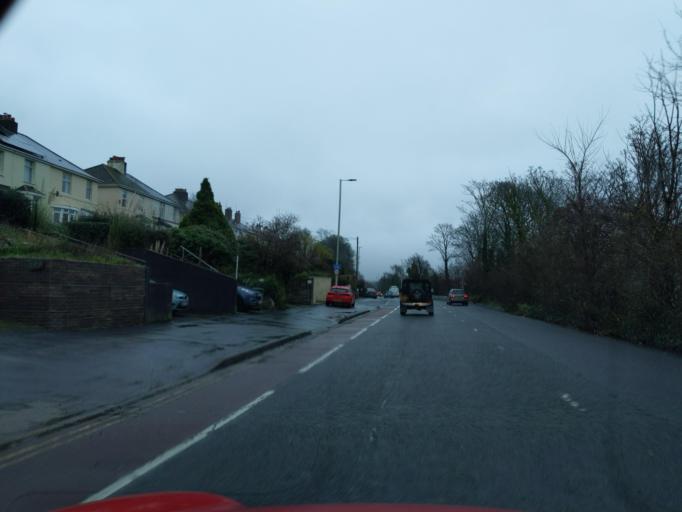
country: GB
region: England
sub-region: Devon
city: Plympton
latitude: 50.3913
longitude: -4.0785
